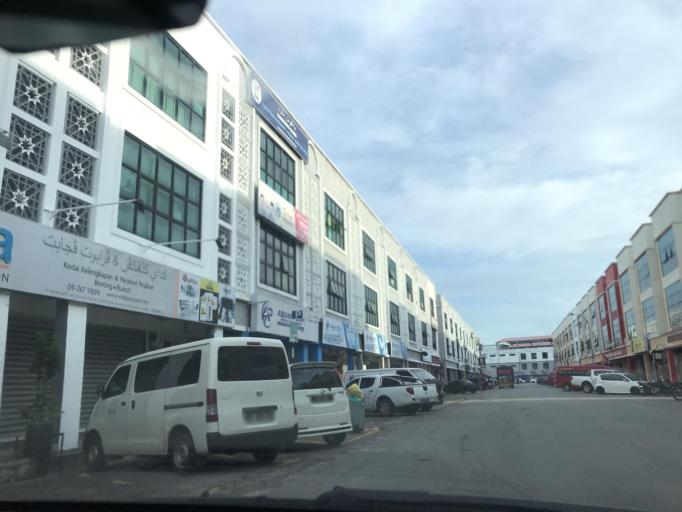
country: MY
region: Kelantan
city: Kota Bharu
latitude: 6.1143
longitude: 102.2332
